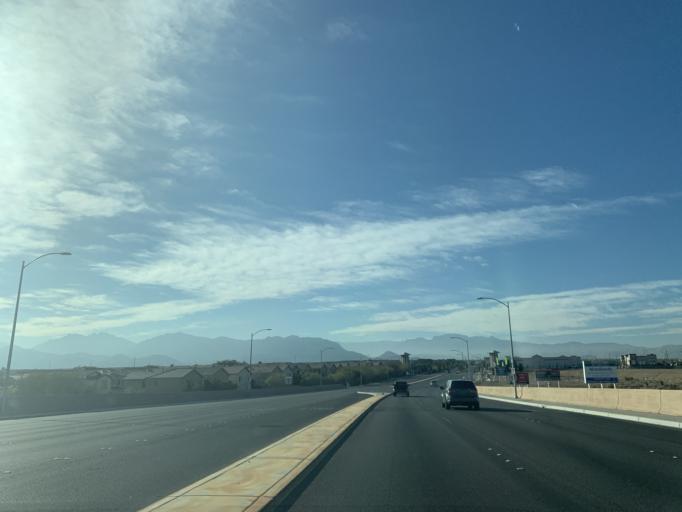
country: US
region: Nevada
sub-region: Clark County
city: Summerlin South
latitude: 36.3143
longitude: -115.3021
